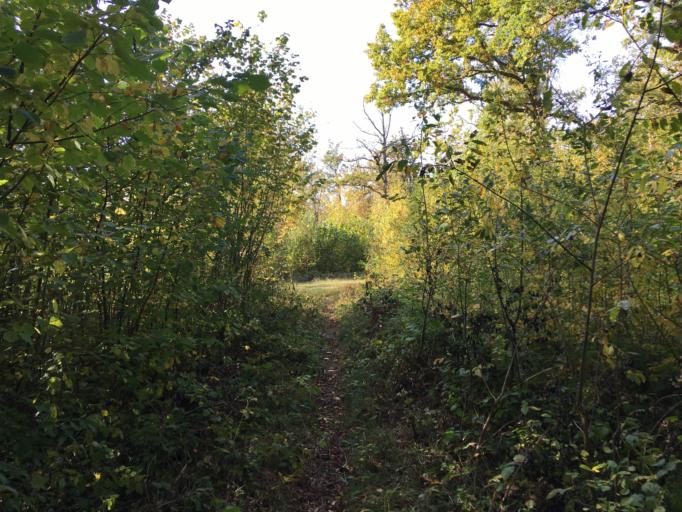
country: SE
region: Kalmar
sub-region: Borgholms Kommun
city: Borgholm
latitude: 56.7478
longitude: 16.6135
